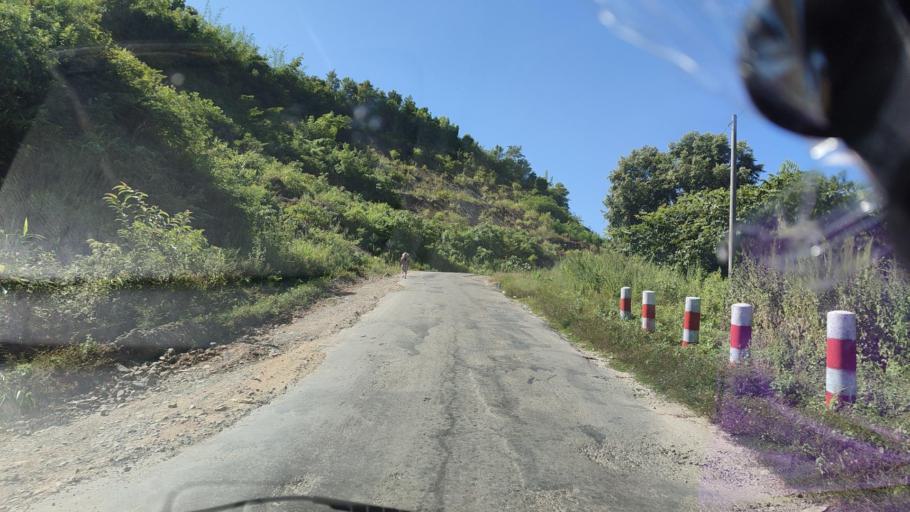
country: MM
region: Rakhine
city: Sittwe
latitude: 19.9821
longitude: 93.6339
